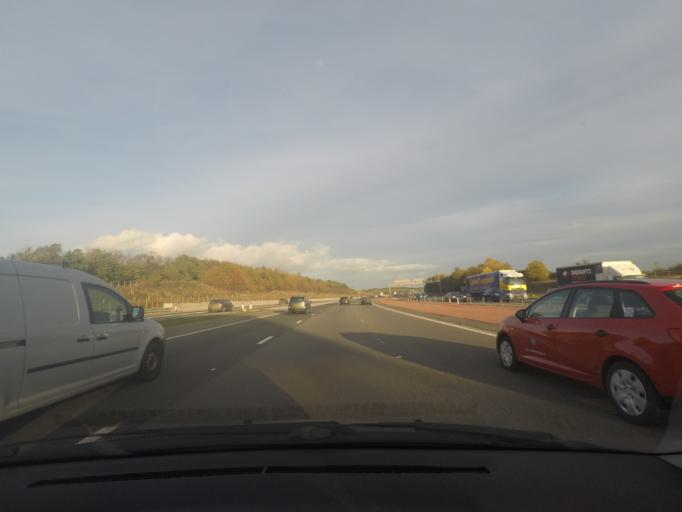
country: GB
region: England
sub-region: City and Borough of Leeds
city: Swillington
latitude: 53.7770
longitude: -1.4658
